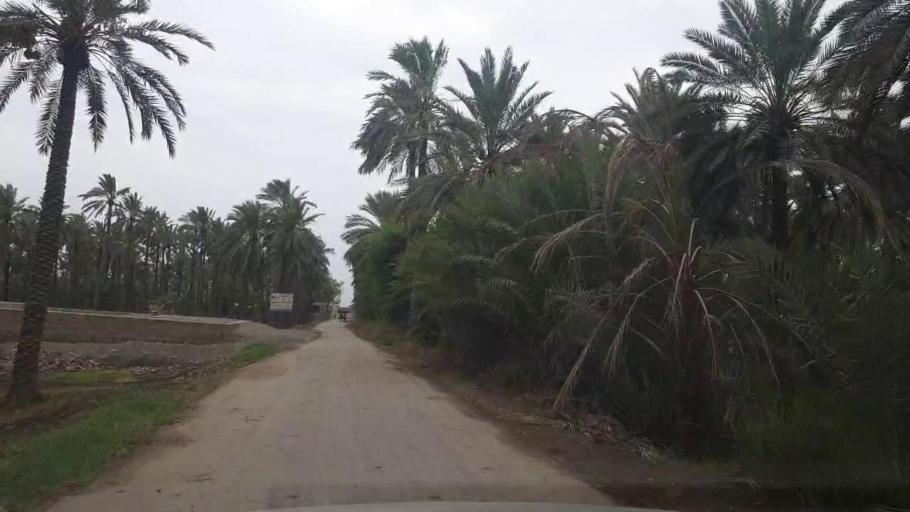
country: PK
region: Sindh
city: Khairpur
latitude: 27.5536
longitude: 68.7507
